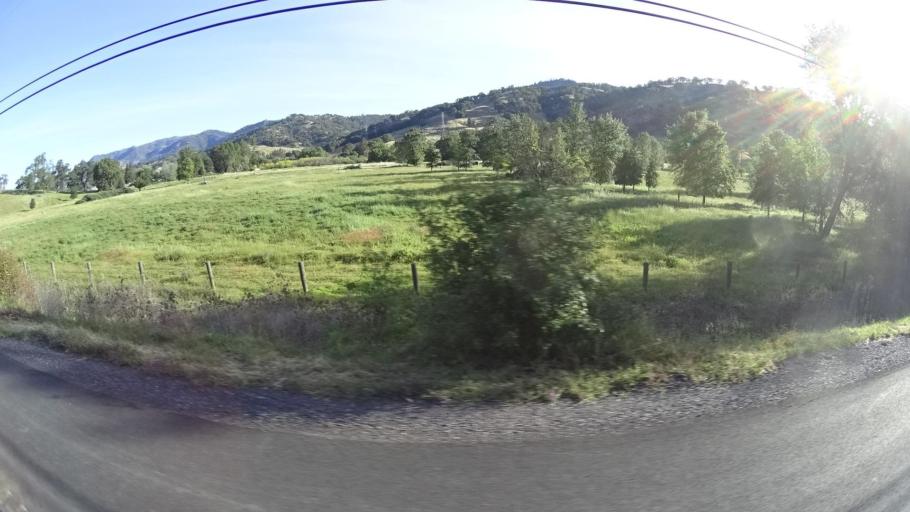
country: US
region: California
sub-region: Lake County
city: Upper Lake
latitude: 39.1738
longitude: -122.9447
